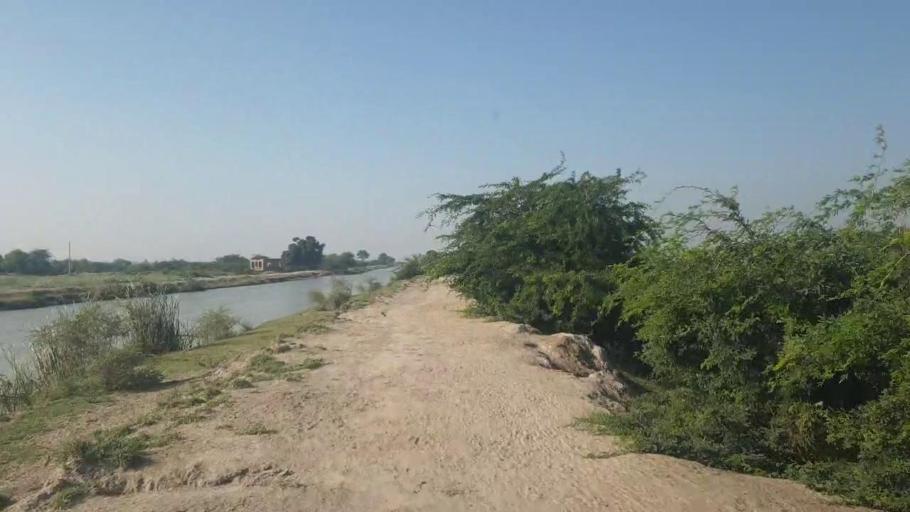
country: PK
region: Sindh
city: Badin
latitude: 24.7076
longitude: 68.8885
